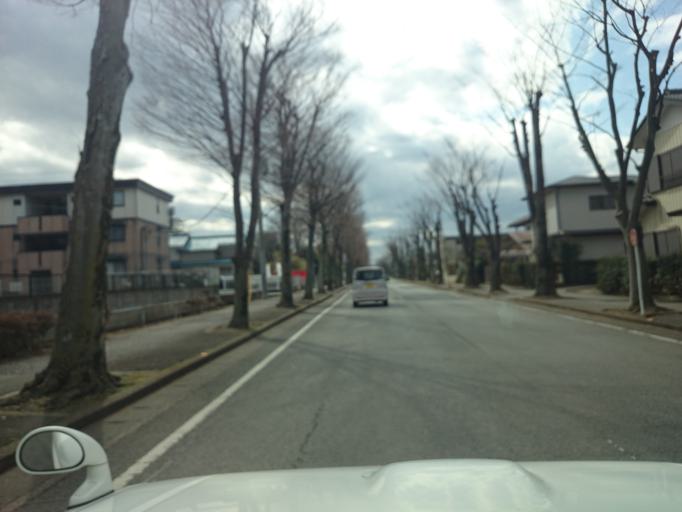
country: JP
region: Saitama
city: Kukichuo
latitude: 36.0662
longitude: 139.6994
